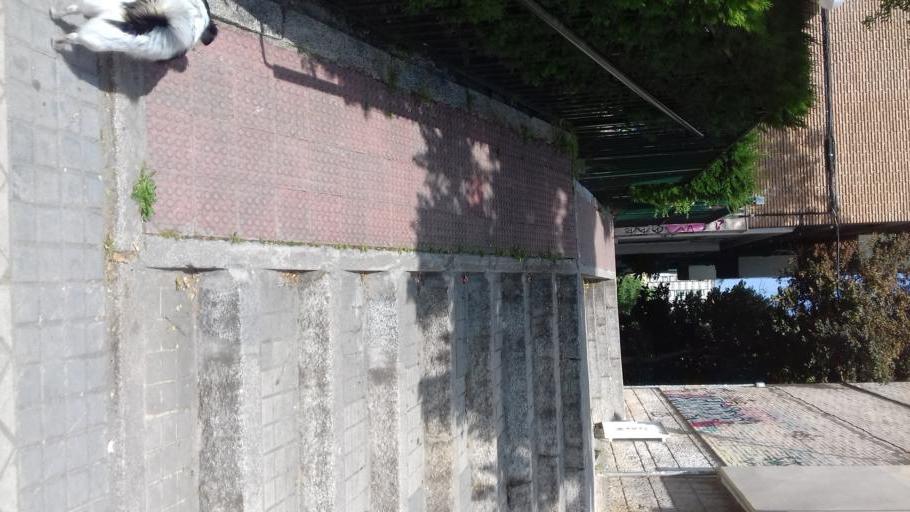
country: ES
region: Madrid
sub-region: Provincia de Madrid
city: Retiro
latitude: 40.4150
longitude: -3.6674
